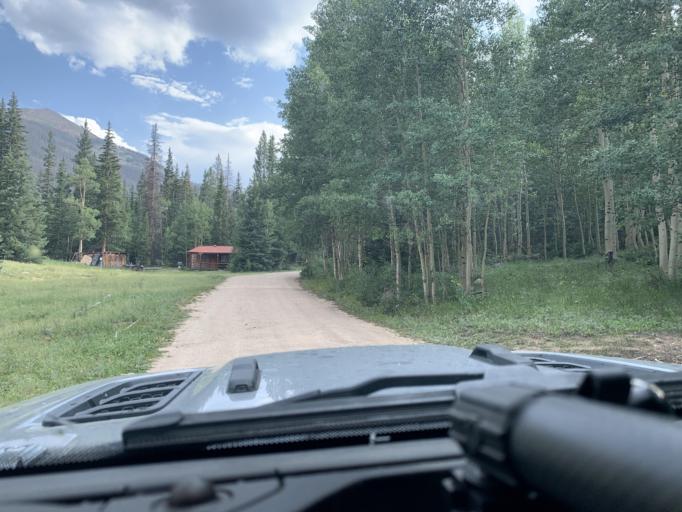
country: US
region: Colorado
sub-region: Chaffee County
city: Buena Vista
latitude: 38.6947
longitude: -106.3515
